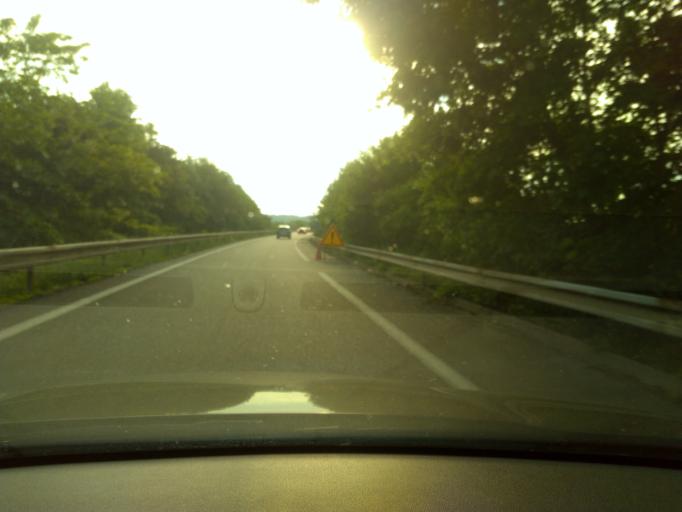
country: FR
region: Lorraine
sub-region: Departement de la Moselle
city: Moulins-les-Metz
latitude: 49.0985
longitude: 6.1220
